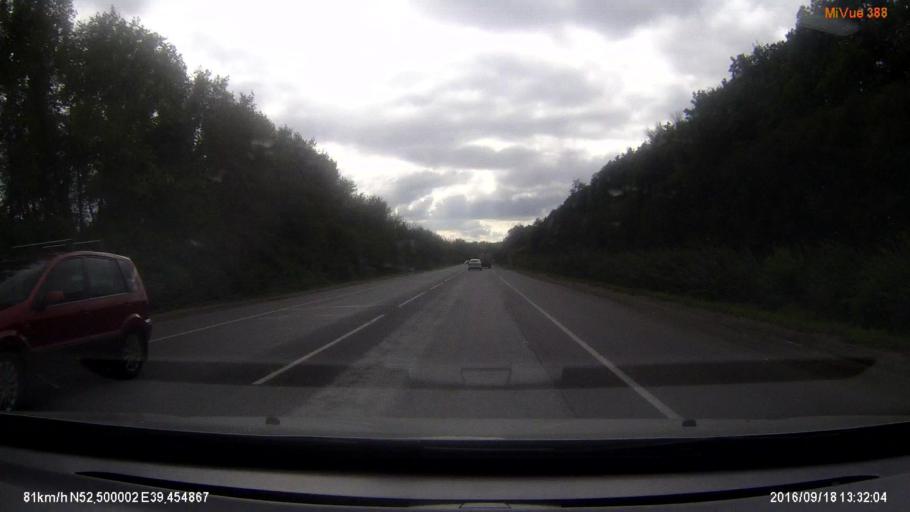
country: RU
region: Lipetsk
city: Borinskoye
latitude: 52.4637
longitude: 39.3934
